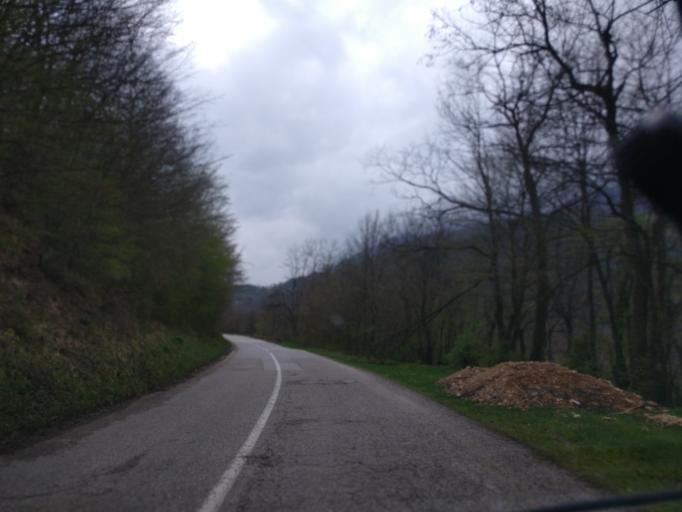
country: BA
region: Republika Srpska
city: Foca
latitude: 43.4601
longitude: 18.7467
